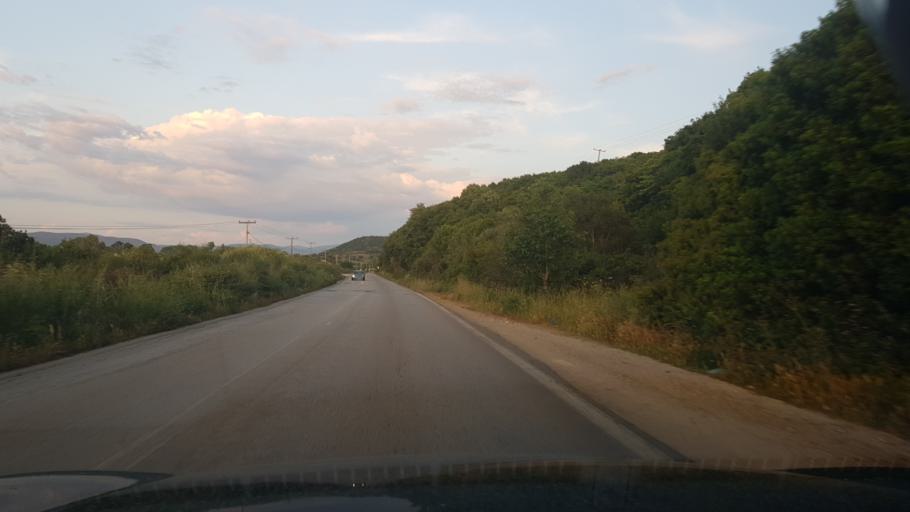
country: GR
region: Ionian Islands
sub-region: Lefkada
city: Lefkada
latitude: 38.8635
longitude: 20.7832
